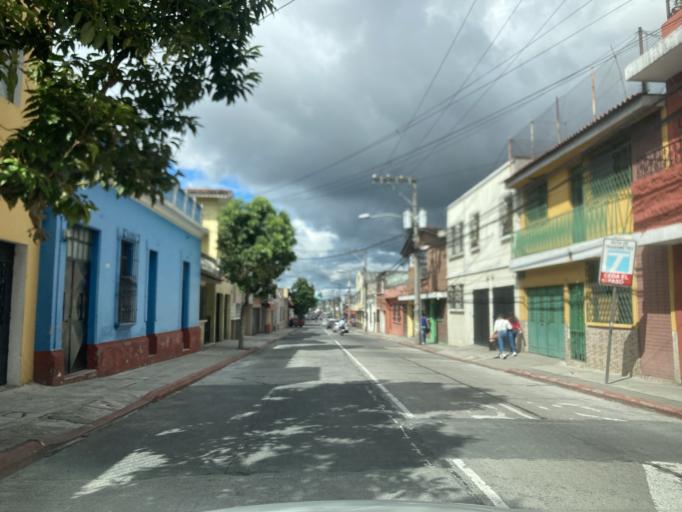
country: GT
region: Guatemala
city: Guatemala City
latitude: 14.6450
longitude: -90.5077
